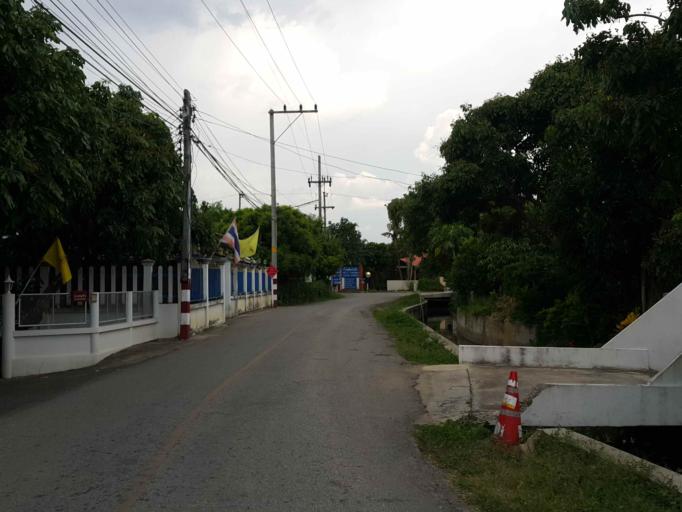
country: TH
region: Chiang Mai
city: Saraphi
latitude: 18.6940
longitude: 99.0270
